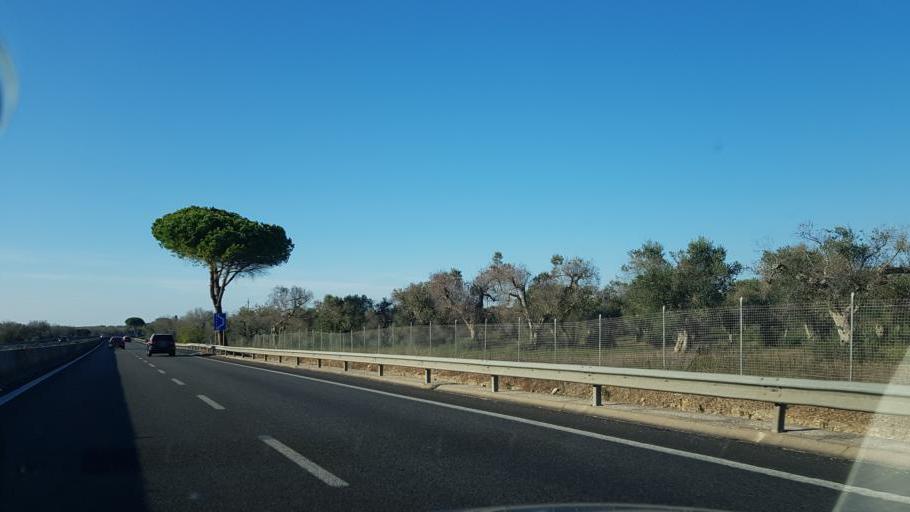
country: IT
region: Apulia
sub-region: Provincia di Lecce
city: Squinzano
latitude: 40.4506
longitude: 18.0682
